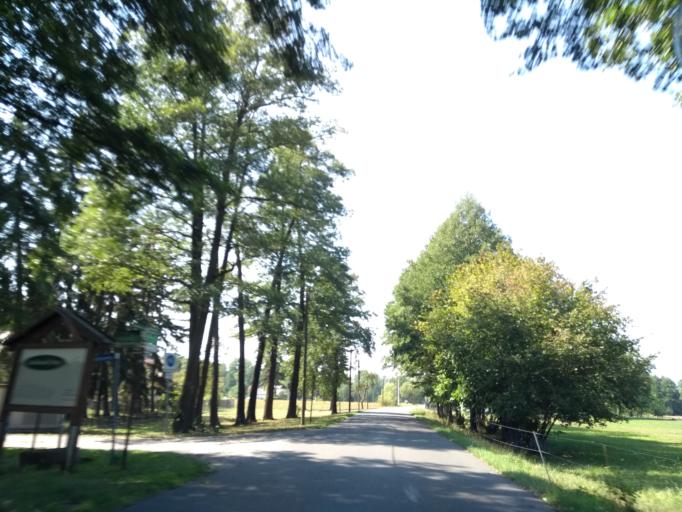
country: DE
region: Brandenburg
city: Burg
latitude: 51.8518
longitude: 14.1176
